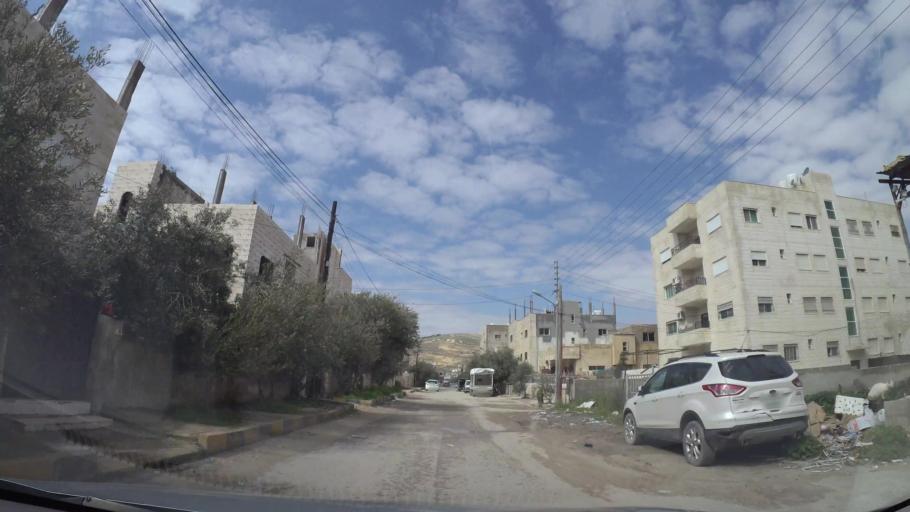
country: JO
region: Amman
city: Al Jubayhah
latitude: 32.0651
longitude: 35.8282
